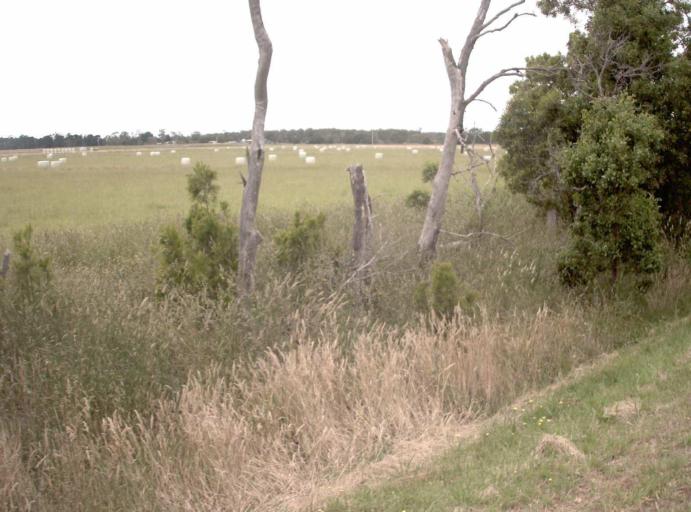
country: AU
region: Victoria
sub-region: Latrobe
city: Traralgon
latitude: -38.4884
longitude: 146.8197
